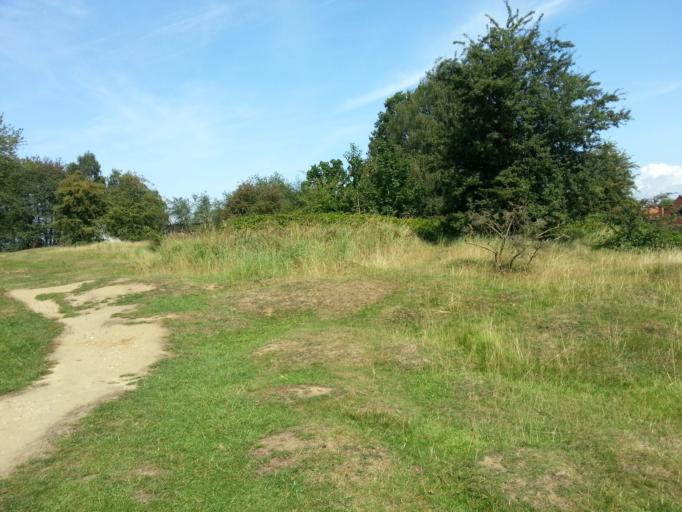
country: BE
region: Flanders
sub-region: Provincie West-Vlaanderen
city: Ieper
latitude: 50.8236
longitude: 2.9305
